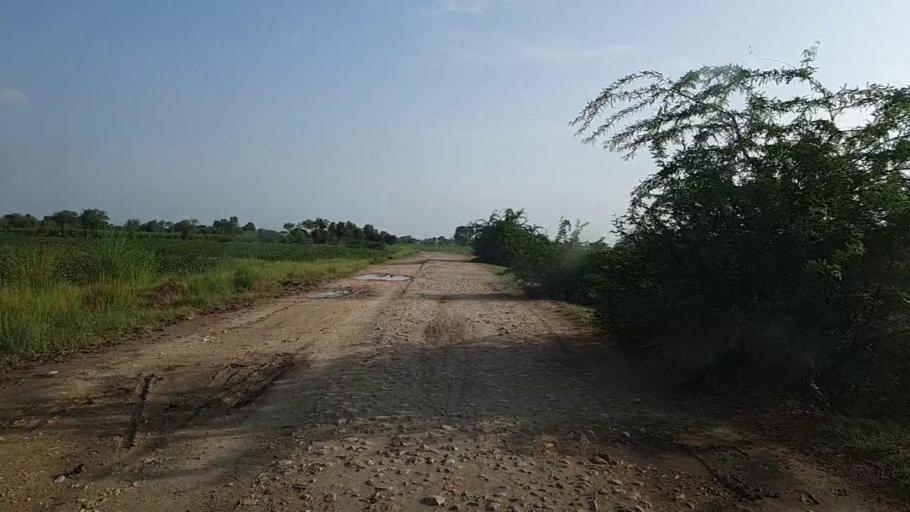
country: PK
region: Sindh
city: Pad Idan
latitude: 26.8119
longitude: 68.2355
